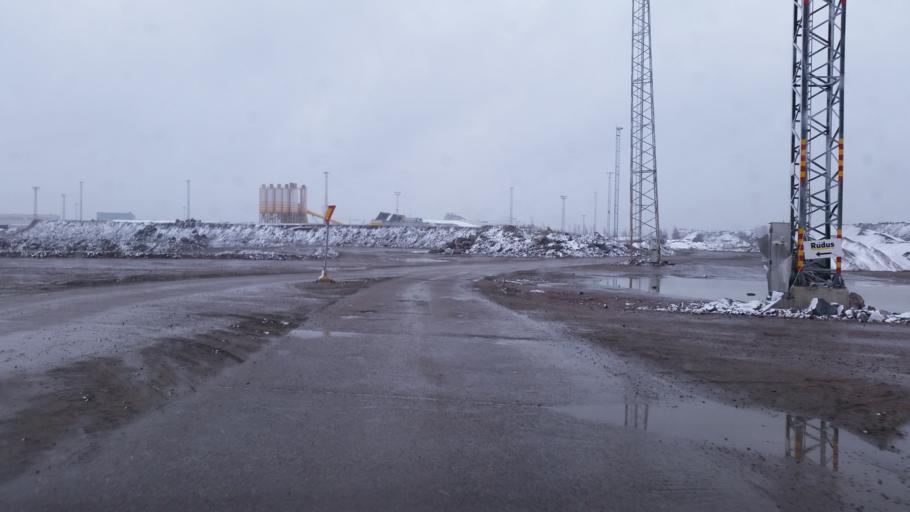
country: FI
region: Uusimaa
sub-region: Helsinki
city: Helsinki
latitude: 60.1553
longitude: 24.9039
